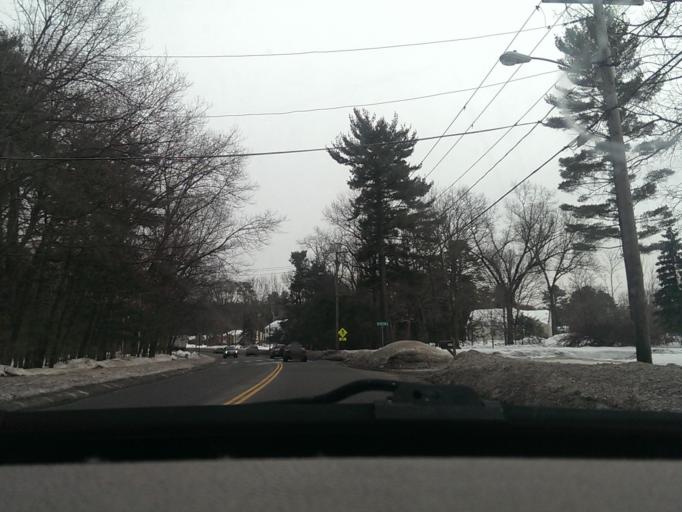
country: US
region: Massachusetts
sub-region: Hampden County
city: Longmeadow
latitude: 42.0632
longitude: -72.5515
